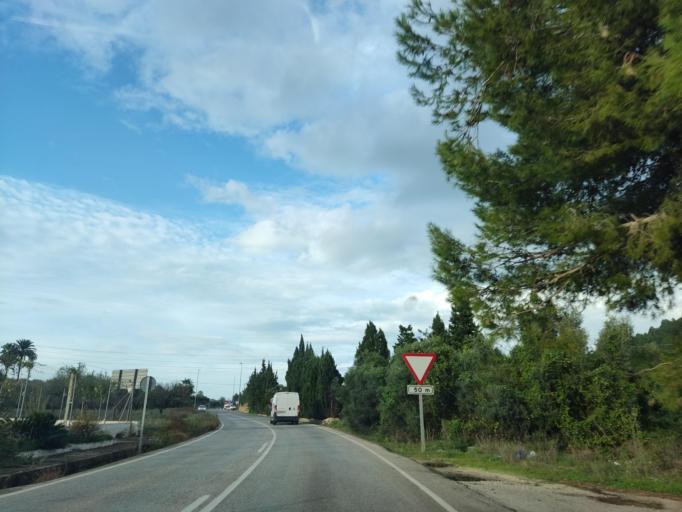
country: ES
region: Valencia
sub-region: Provincia de Alicante
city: Pedreguer
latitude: 38.8054
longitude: 0.0337
